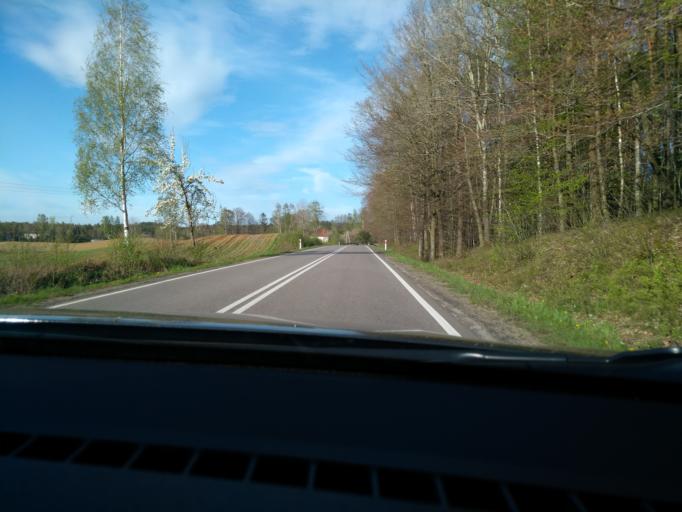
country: PL
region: Pomeranian Voivodeship
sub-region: Powiat leborski
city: Cewice
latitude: 54.3379
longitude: 17.7370
